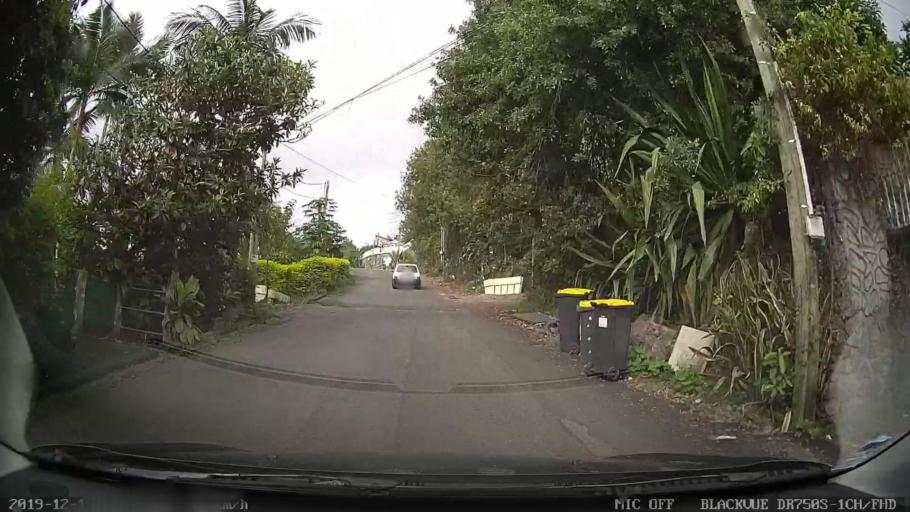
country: RE
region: Reunion
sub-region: Reunion
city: Le Tampon
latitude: -21.2549
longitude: 55.5167
